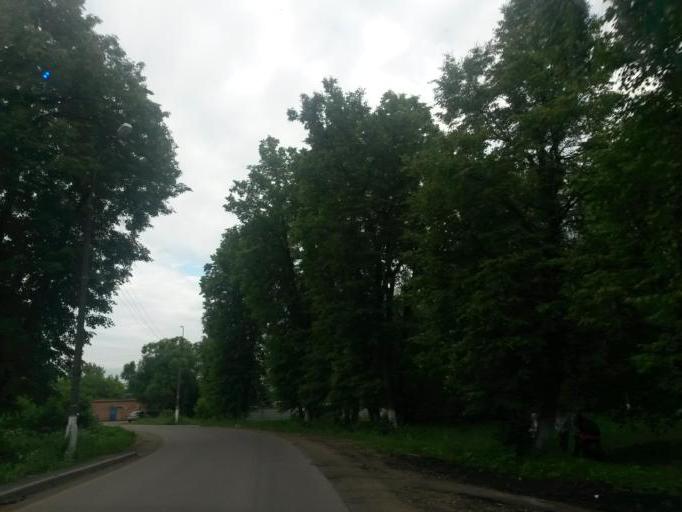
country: RU
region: Moskovskaya
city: Lyubuchany
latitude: 55.2476
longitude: 37.6272
